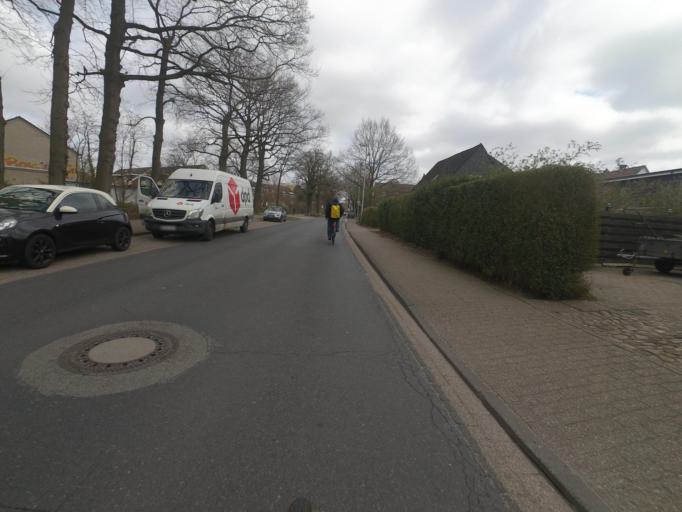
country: DE
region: Lower Saxony
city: Oldenburg
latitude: 53.1326
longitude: 8.1625
